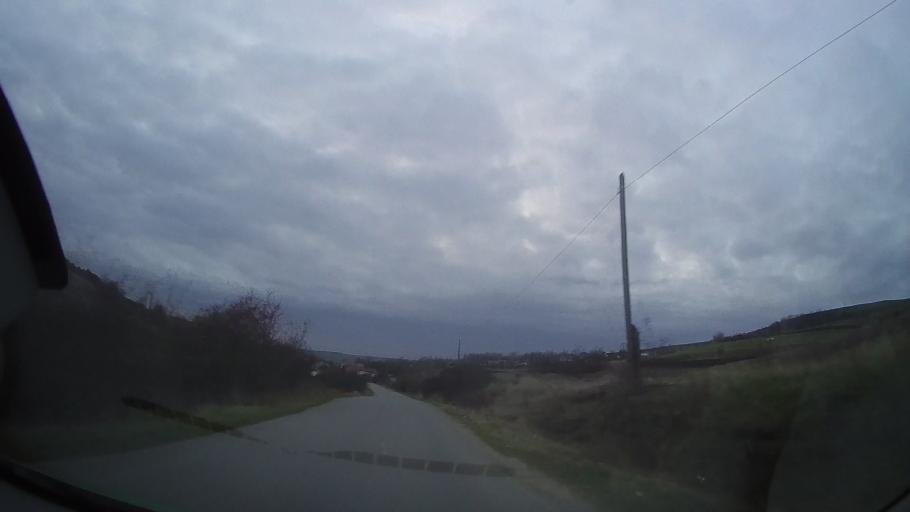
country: RO
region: Cluj
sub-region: Comuna Caianu
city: Vaida-Camaras
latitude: 46.8338
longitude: 23.9593
